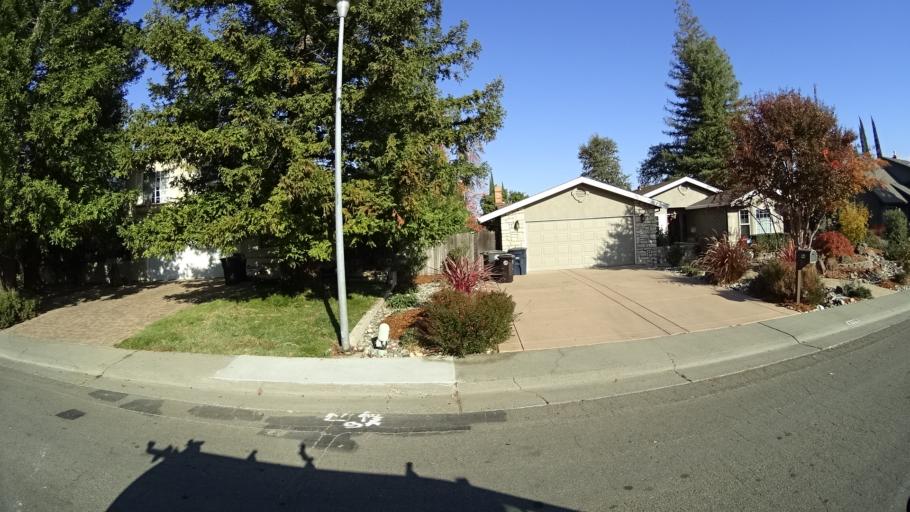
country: US
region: California
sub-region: Sacramento County
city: Citrus Heights
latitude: 38.7163
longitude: -121.2574
